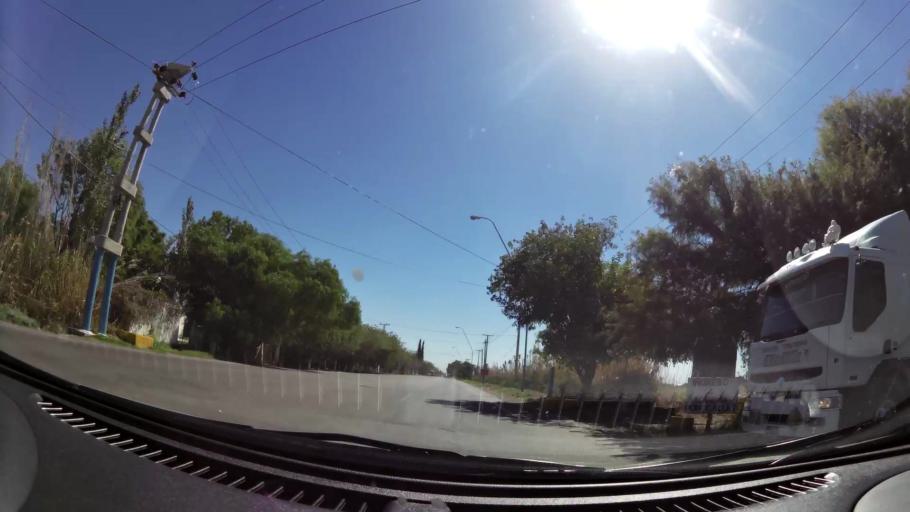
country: AR
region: San Juan
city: Villa Krause
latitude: -31.6015
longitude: -68.5423
